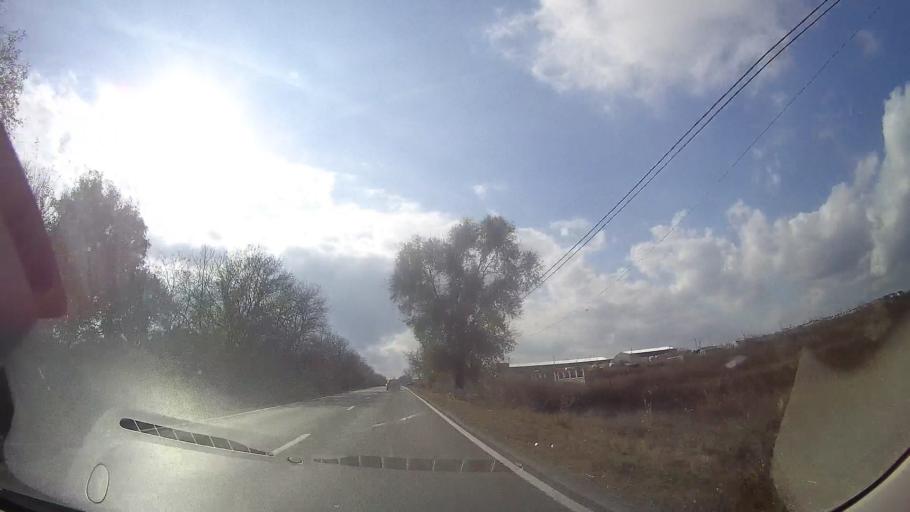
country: RO
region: Constanta
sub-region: Comuna Agigea
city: Agigea
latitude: 44.0838
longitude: 28.6063
